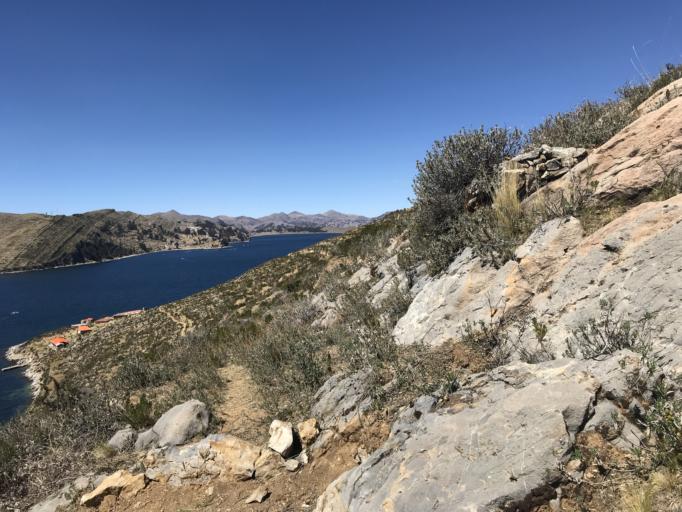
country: BO
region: La Paz
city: Yumani
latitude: -16.0492
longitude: -69.1451
